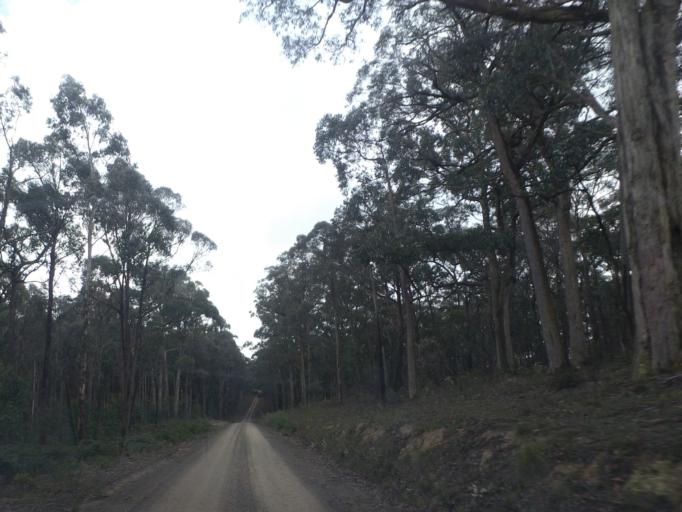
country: AU
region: Victoria
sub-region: Moorabool
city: Bacchus Marsh
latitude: -37.4374
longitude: 144.3203
